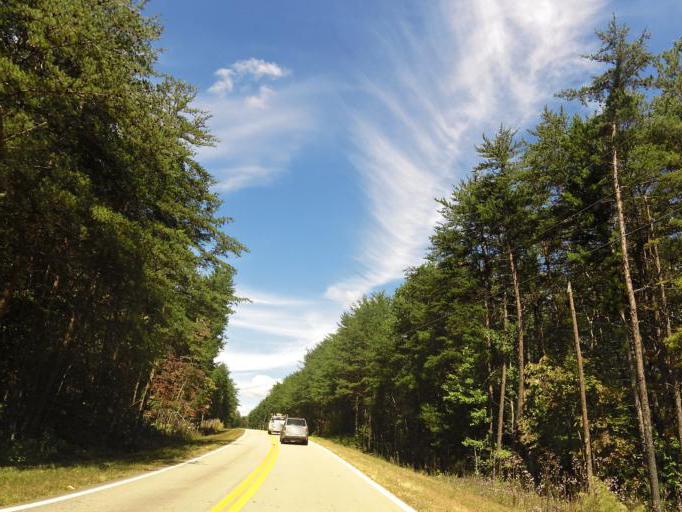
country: US
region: Georgia
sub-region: Pickens County
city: Nelson
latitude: 34.4823
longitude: -84.2576
